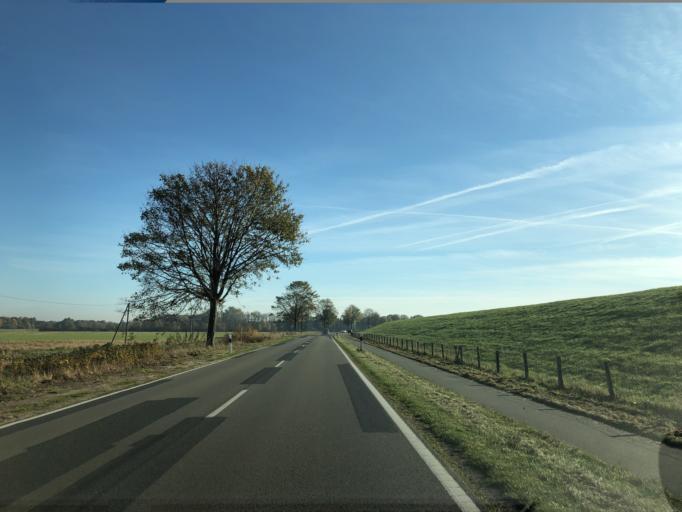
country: DE
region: Lower Saxony
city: Rhede
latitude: 53.0571
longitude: 7.3087
